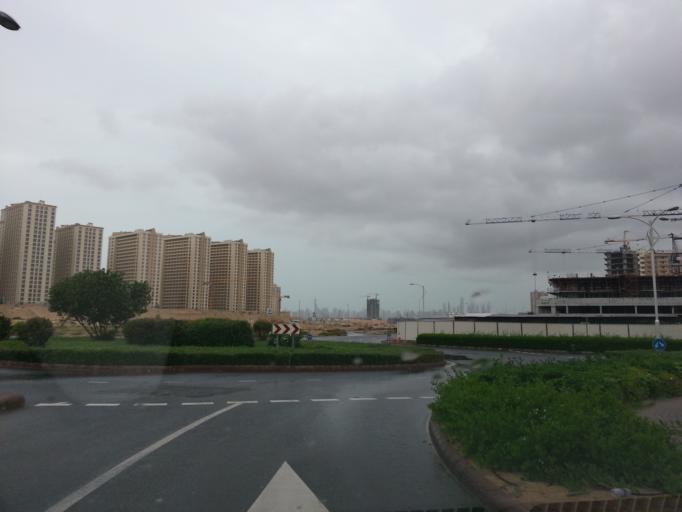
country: AE
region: Dubai
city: Dubai
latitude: 25.0344
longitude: 55.2072
